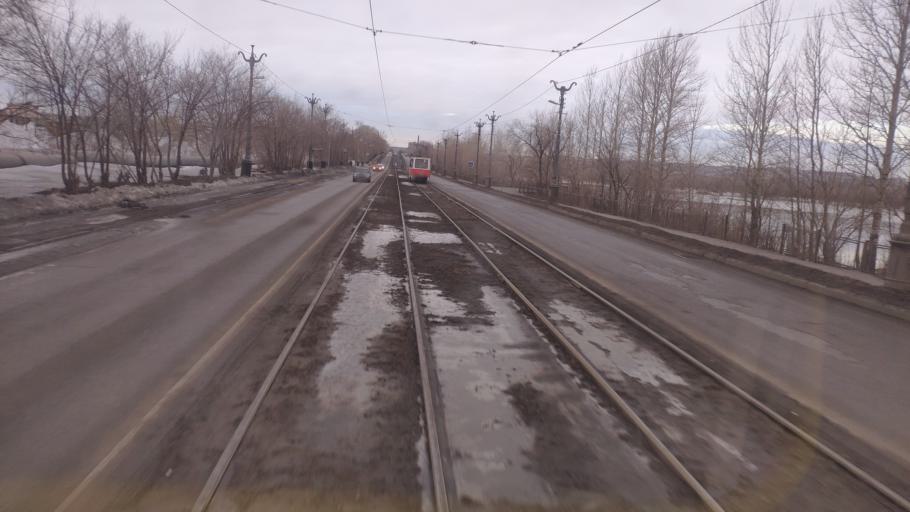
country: RU
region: Chelyabinsk
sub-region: Gorod Magnitogorsk
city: Magnitogorsk
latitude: 53.4222
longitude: 59.0176
